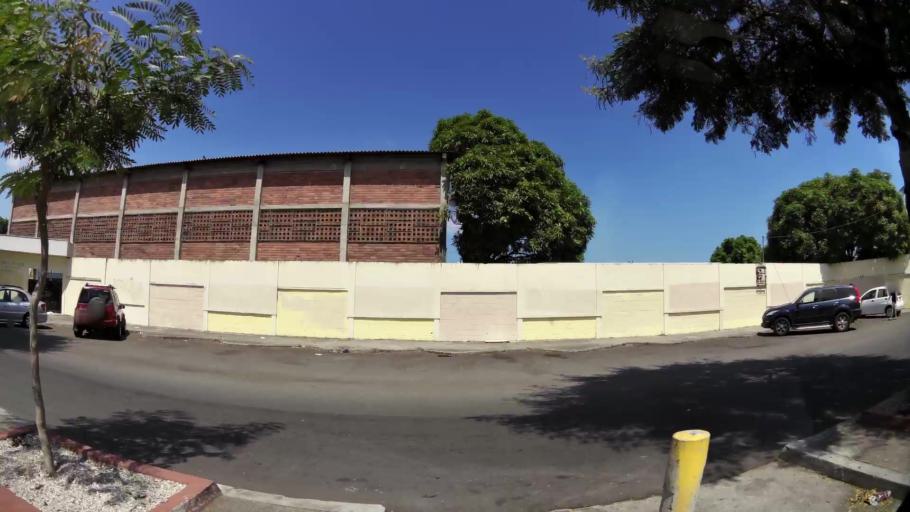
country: EC
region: Guayas
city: Guayaquil
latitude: -2.2321
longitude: -79.9013
